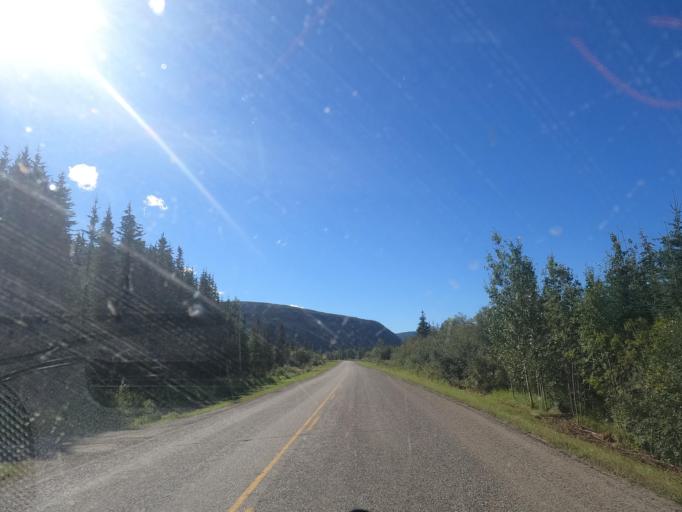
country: CA
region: Yukon
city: Dawson City
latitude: 64.0619
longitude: -139.0104
